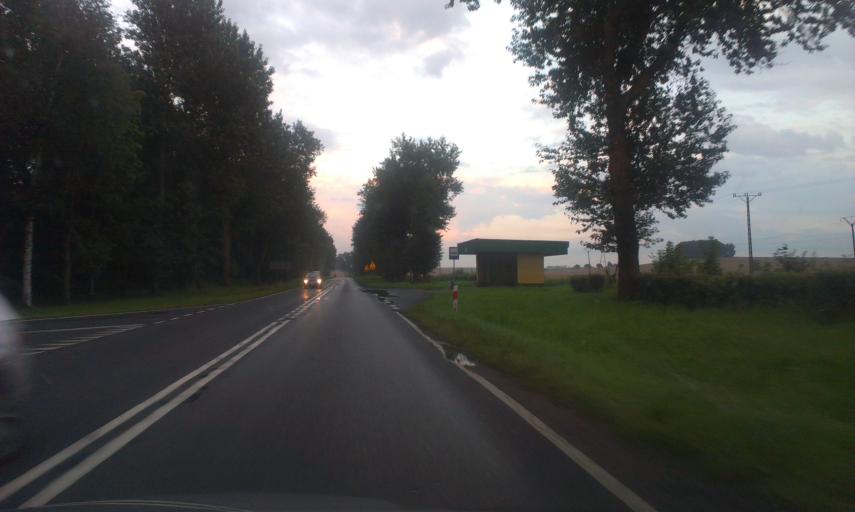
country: PL
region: West Pomeranian Voivodeship
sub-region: Koszalin
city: Koszalin
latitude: 54.1495
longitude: 16.2443
